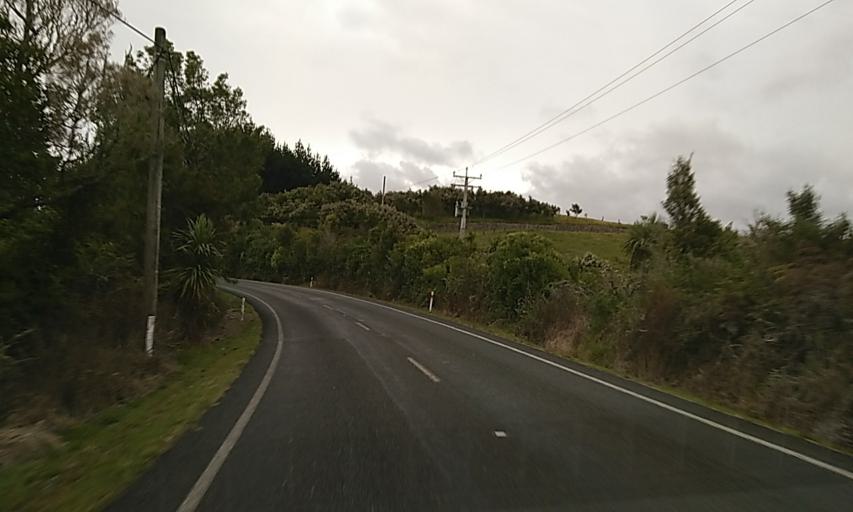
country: NZ
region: Auckland
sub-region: Auckland
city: Pukekohe East
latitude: -37.3067
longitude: 174.9368
